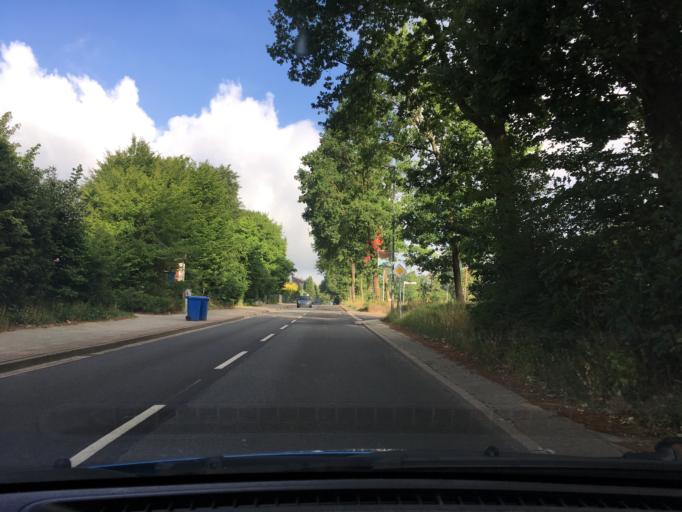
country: DE
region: Lower Saxony
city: Buchholz in der Nordheide
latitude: 53.3249
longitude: 9.8482
